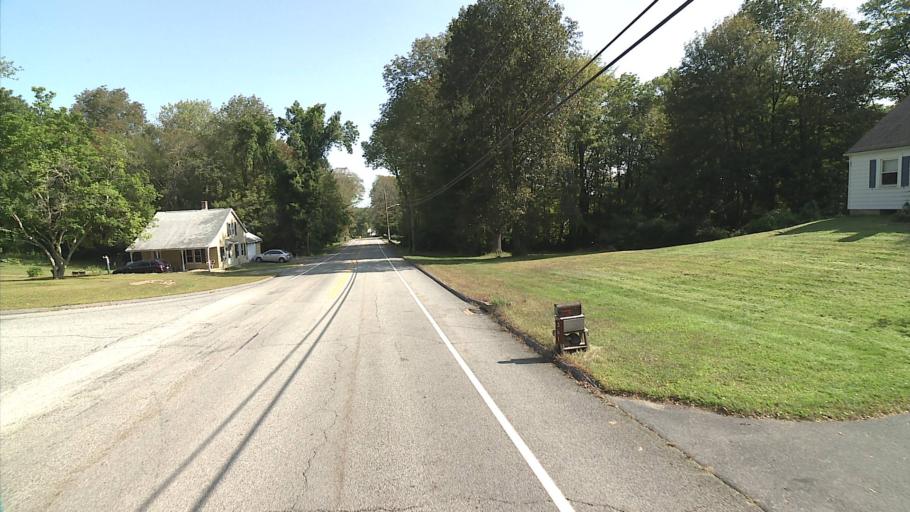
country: US
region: Connecticut
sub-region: Windham County
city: Wauregan
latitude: 41.7377
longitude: -71.9638
